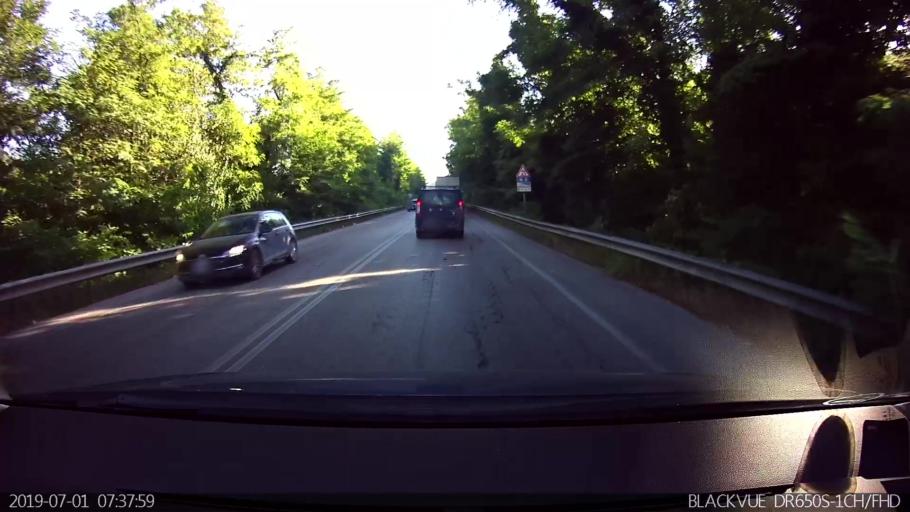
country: IT
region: Latium
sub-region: Provincia di Frosinone
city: Giuliano di Roma
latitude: 41.5413
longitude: 13.2677
